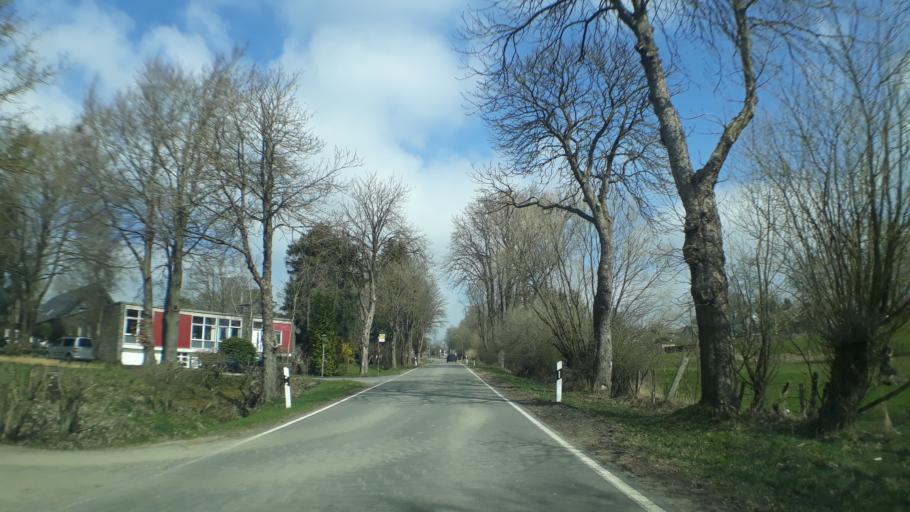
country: DE
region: North Rhine-Westphalia
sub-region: Regierungsbezirk Koln
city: Monschau
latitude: 50.5666
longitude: 6.2605
